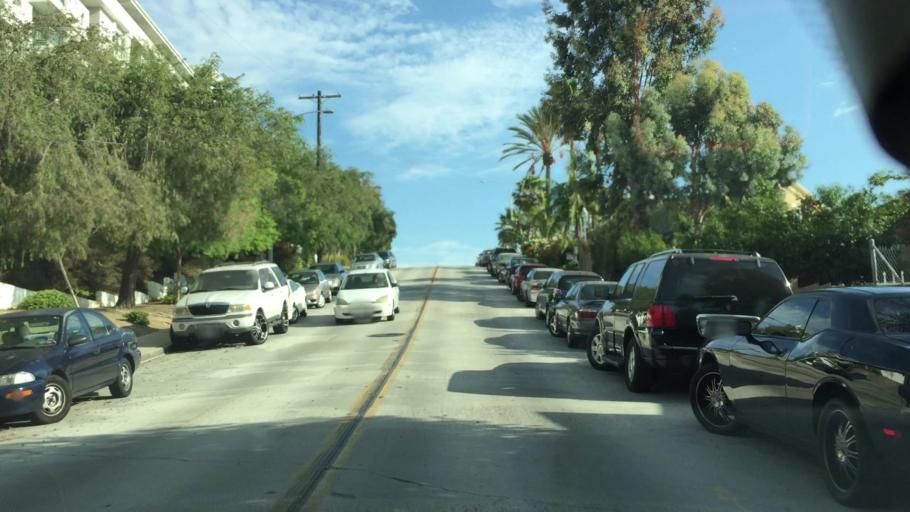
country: US
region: California
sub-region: San Diego County
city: Lemon Grove
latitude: 32.7543
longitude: -117.0837
